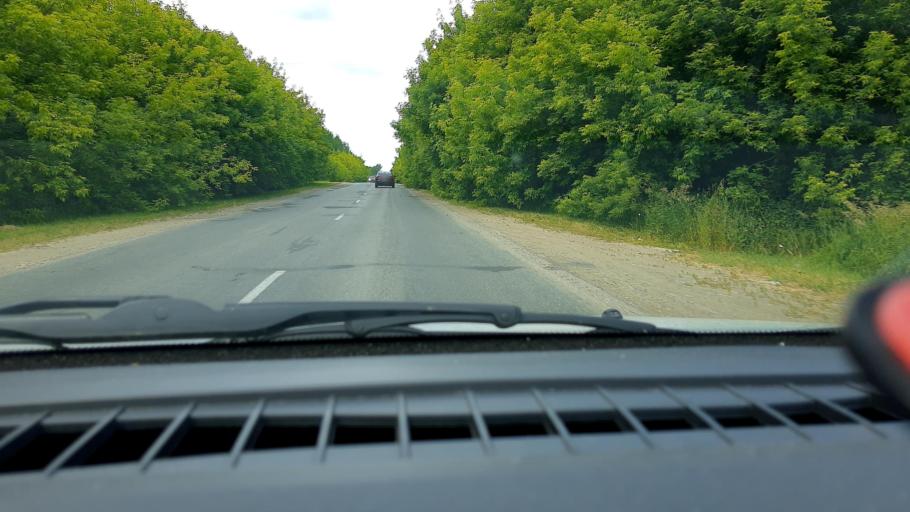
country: RU
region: Nizjnij Novgorod
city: Kstovo
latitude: 56.1317
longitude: 44.1026
